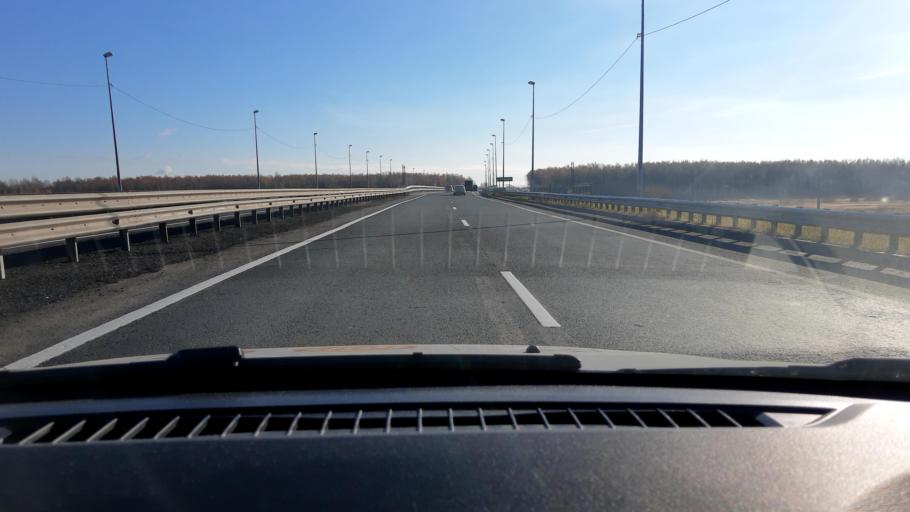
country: RU
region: Nizjnij Novgorod
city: Burevestnik
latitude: 56.1232
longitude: 43.8039
